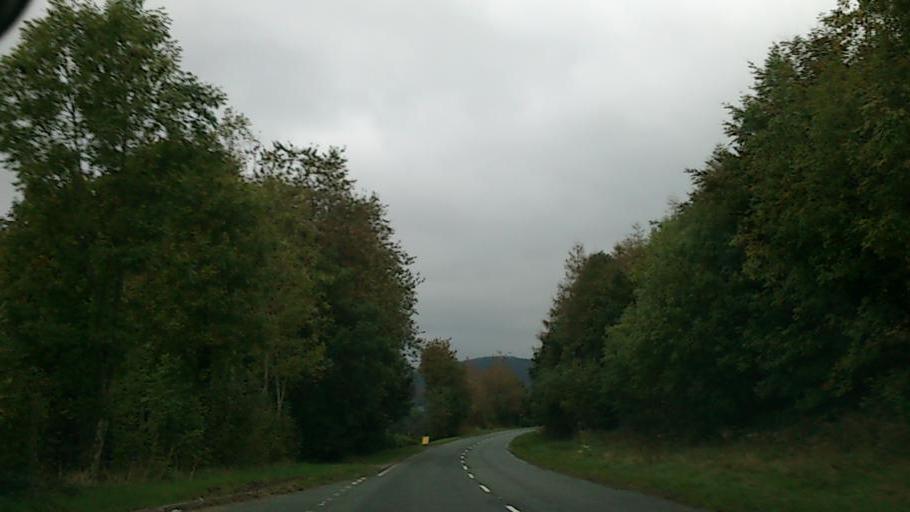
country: GB
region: Wales
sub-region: Gwynedd
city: Corris
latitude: 52.6651
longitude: -3.7077
